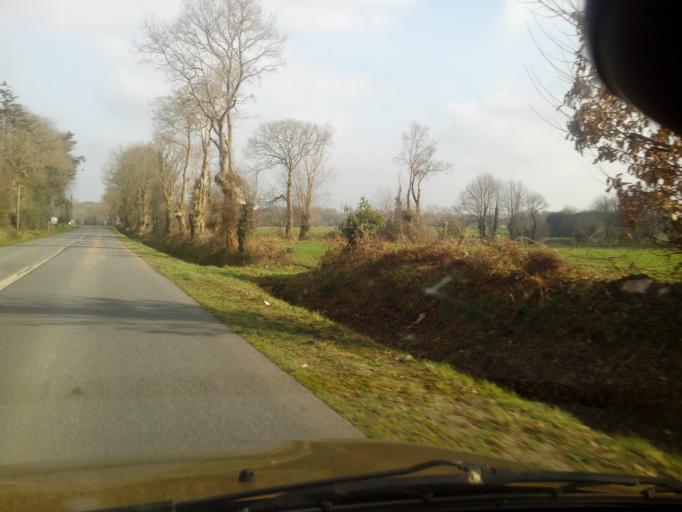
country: FR
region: Brittany
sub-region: Departement du Morbihan
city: Questembert
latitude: 47.6901
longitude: -2.4751
